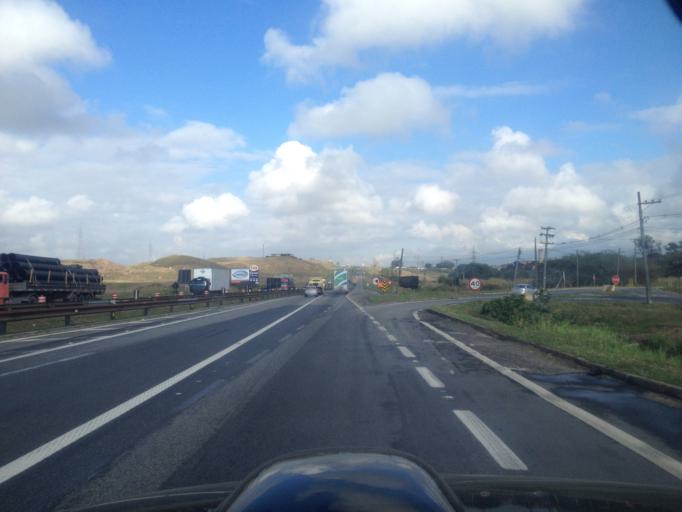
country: BR
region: Rio de Janeiro
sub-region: Resende
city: Resende
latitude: -22.4537
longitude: -44.3732
